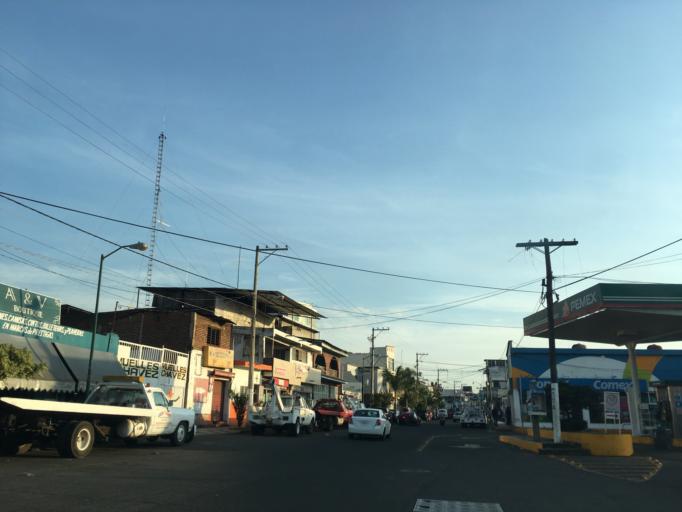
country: MX
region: Michoacan
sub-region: Los Reyes
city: La Higuerita (Colonia San Rafael)
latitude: 19.5941
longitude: -102.4727
